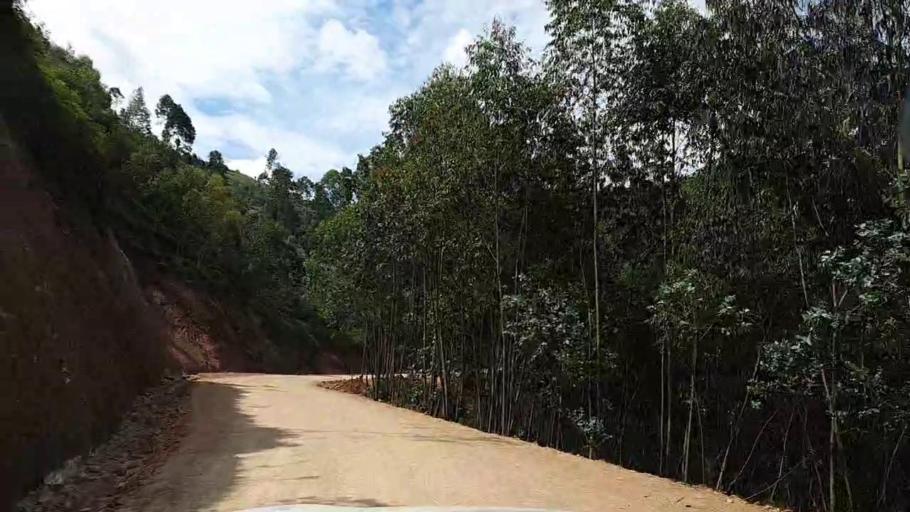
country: RW
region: Southern Province
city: Nzega
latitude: -2.3395
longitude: 29.4386
